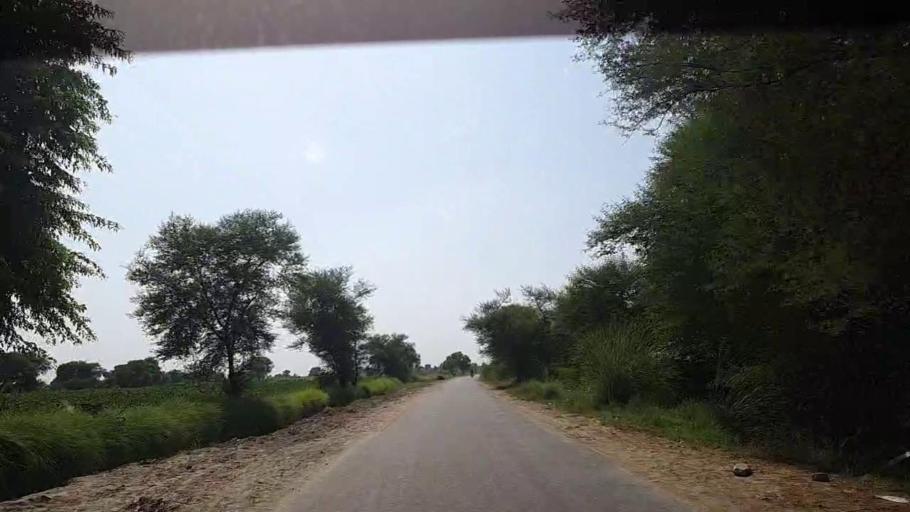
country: PK
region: Sindh
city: Khanpur
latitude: 27.8433
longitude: 69.4082
